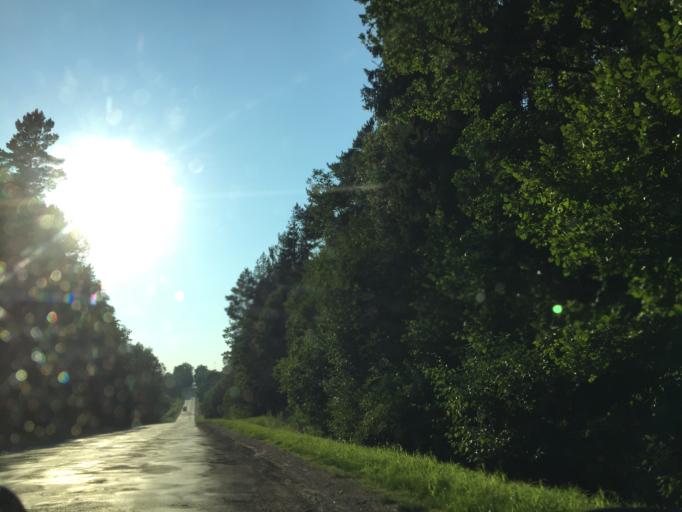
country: LV
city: Tervete
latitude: 56.4329
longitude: 23.5333
